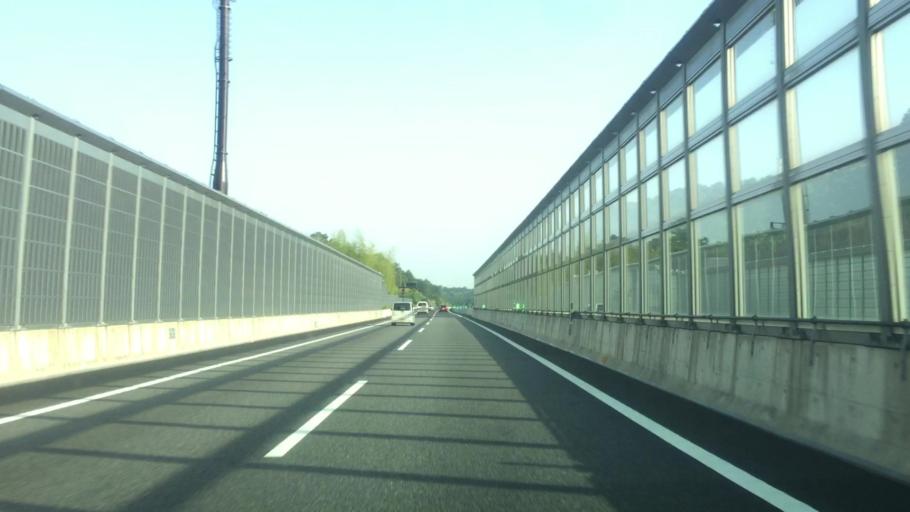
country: JP
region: Aichi
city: Okazaki
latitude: 34.9752
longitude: 137.2455
